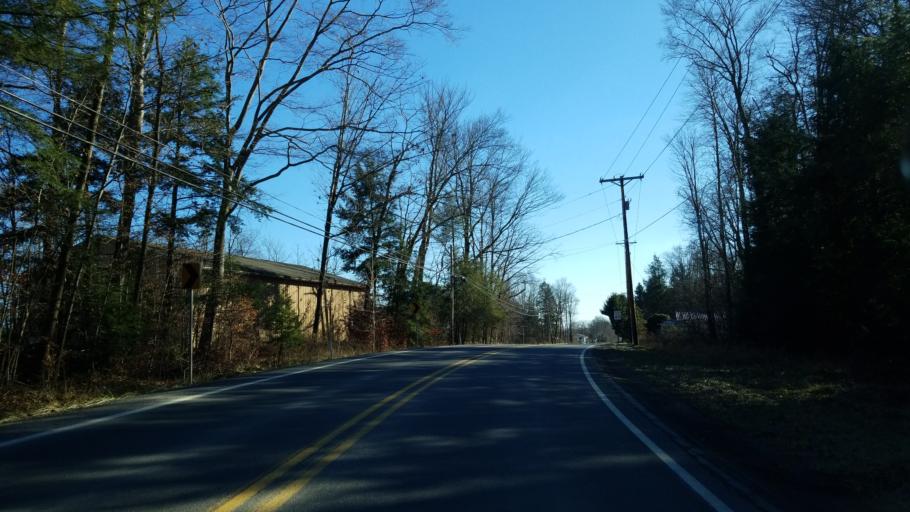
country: US
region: Pennsylvania
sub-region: Jefferson County
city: Falls Creek
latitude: 41.1745
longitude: -78.8356
